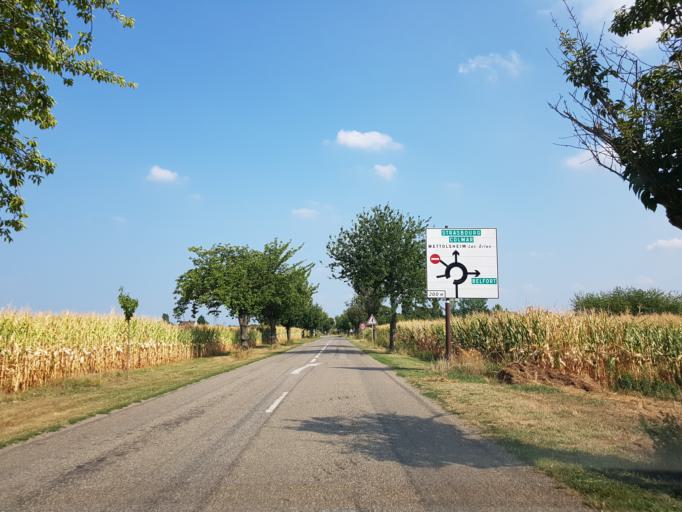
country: FR
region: Alsace
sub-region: Departement du Haut-Rhin
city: Eguisheim
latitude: 48.0408
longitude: 7.3172
